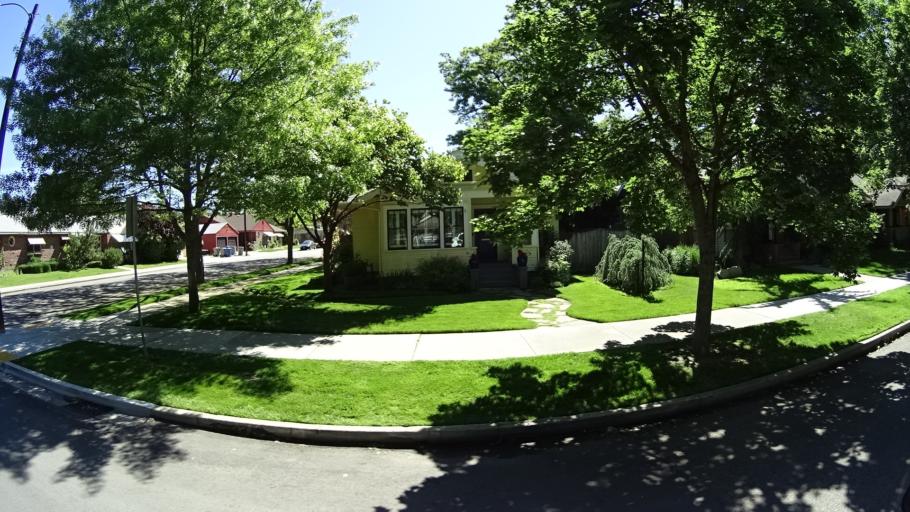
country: US
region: Idaho
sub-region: Ada County
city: Boise
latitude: 43.6311
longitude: -116.2134
